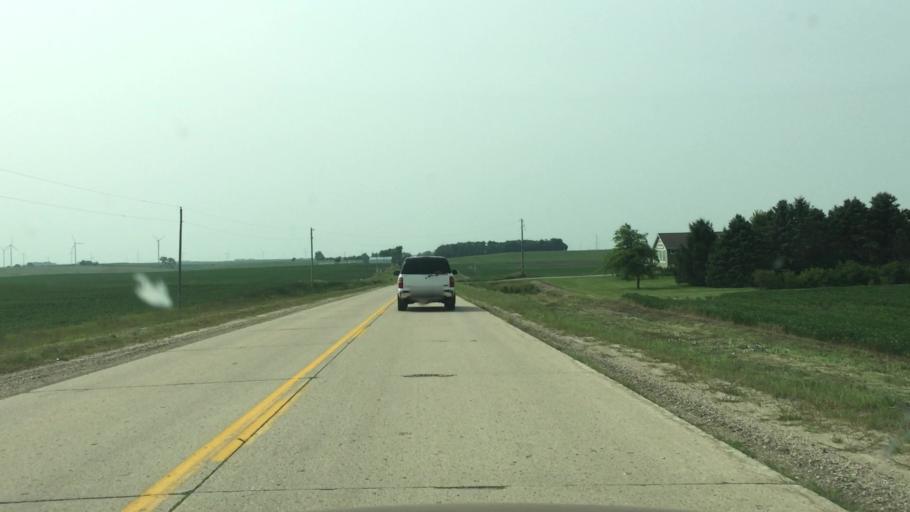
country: US
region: Iowa
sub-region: Dickinson County
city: Lake Park
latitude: 43.4296
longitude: -95.2891
